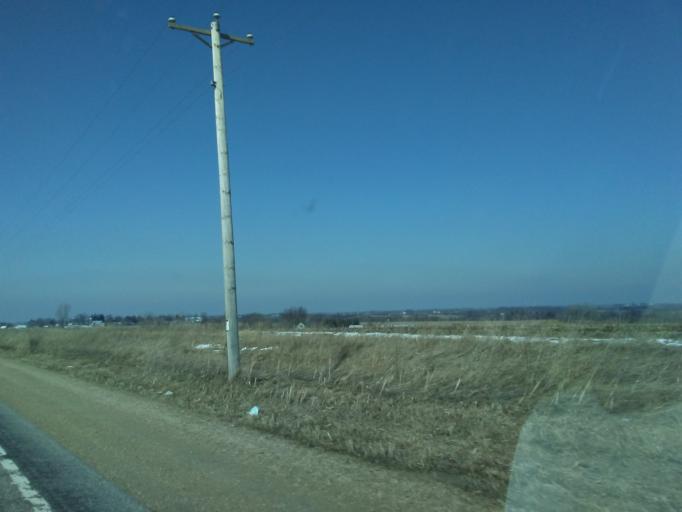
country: US
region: Wisconsin
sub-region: Vernon County
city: Westby
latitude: 43.6647
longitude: -90.8670
